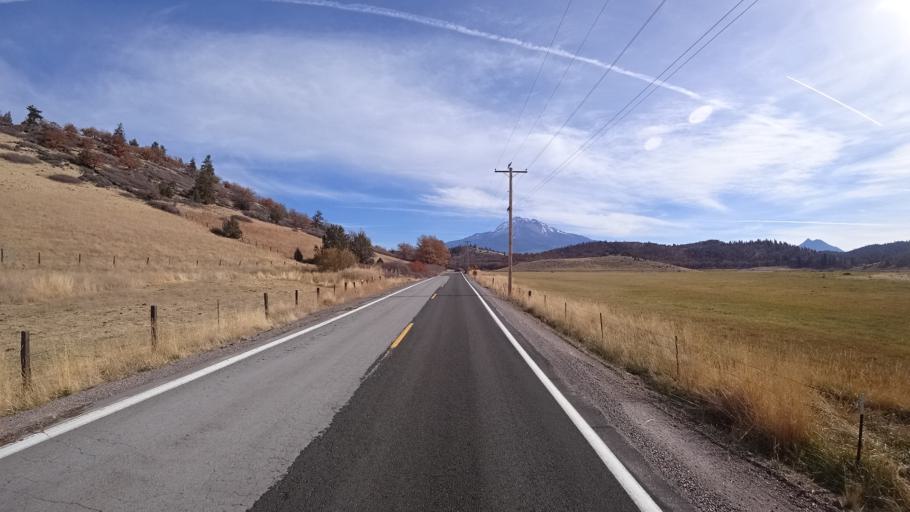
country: US
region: California
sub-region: Siskiyou County
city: Weed
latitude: 41.4681
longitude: -122.4305
